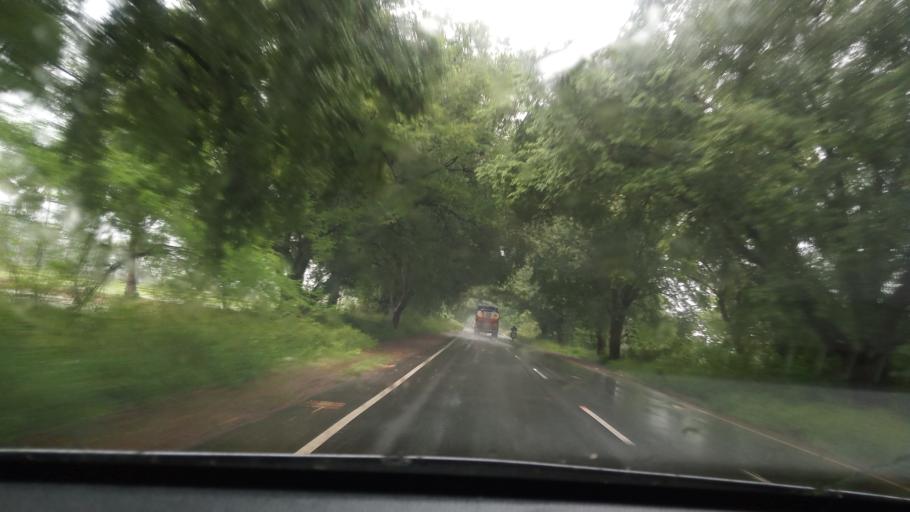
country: IN
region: Tamil Nadu
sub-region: Vellore
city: Kalavai
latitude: 12.8148
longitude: 79.4119
